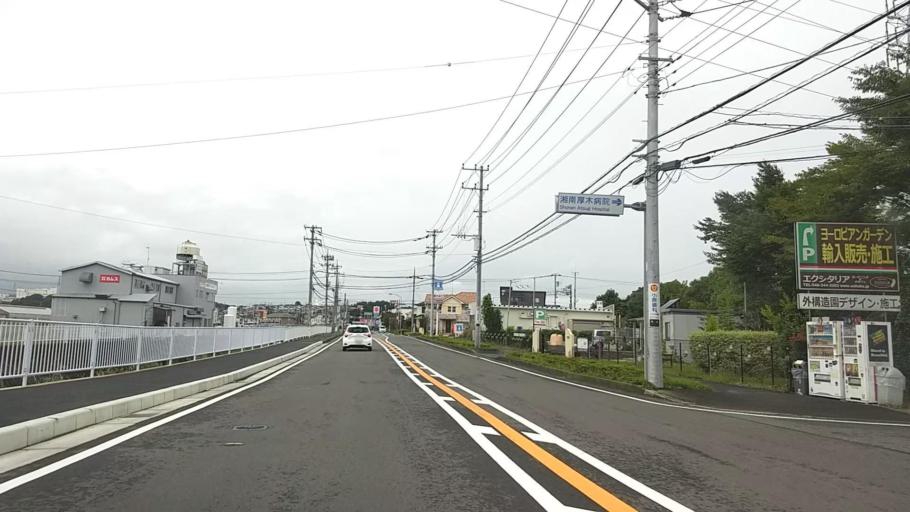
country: JP
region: Kanagawa
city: Atsugi
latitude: 35.4330
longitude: 139.3526
